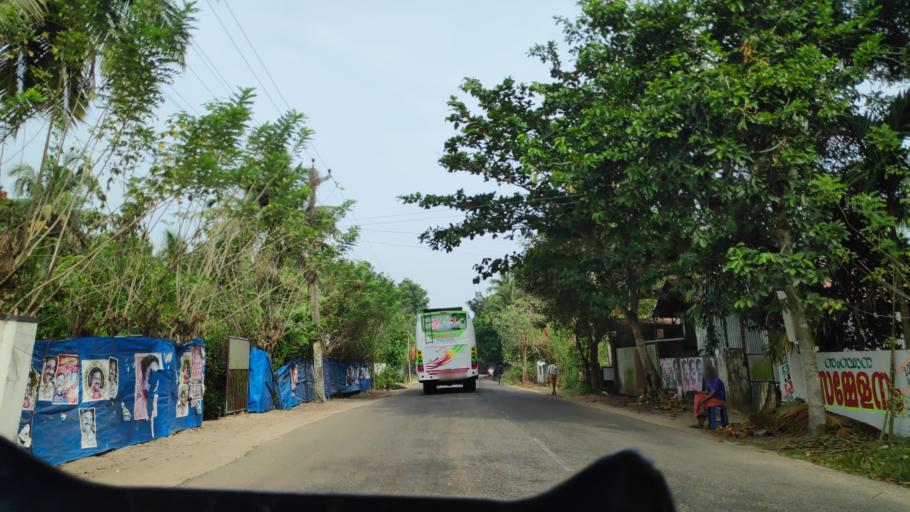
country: IN
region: Kerala
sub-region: Alappuzha
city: Kutiatodu
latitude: 9.8141
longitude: 76.3517
